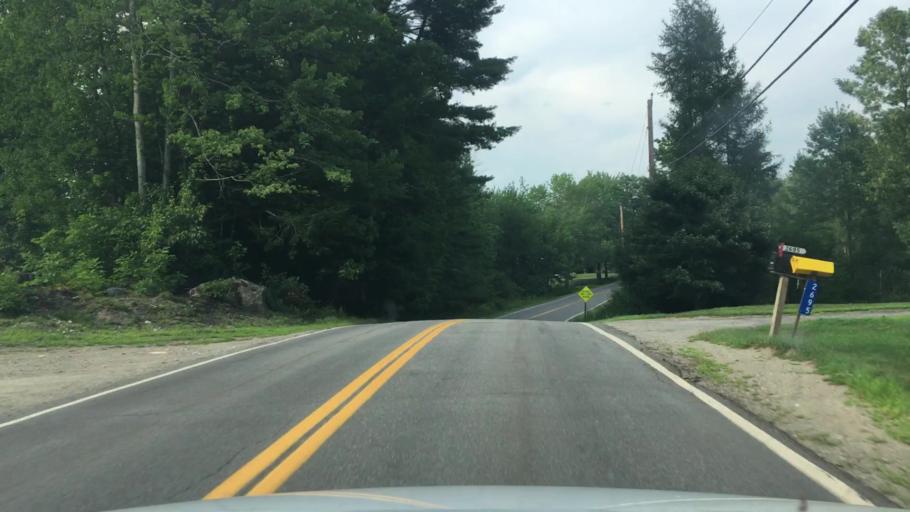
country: US
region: Maine
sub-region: Lincoln County
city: Waldoboro
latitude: 44.1748
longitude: -69.3785
